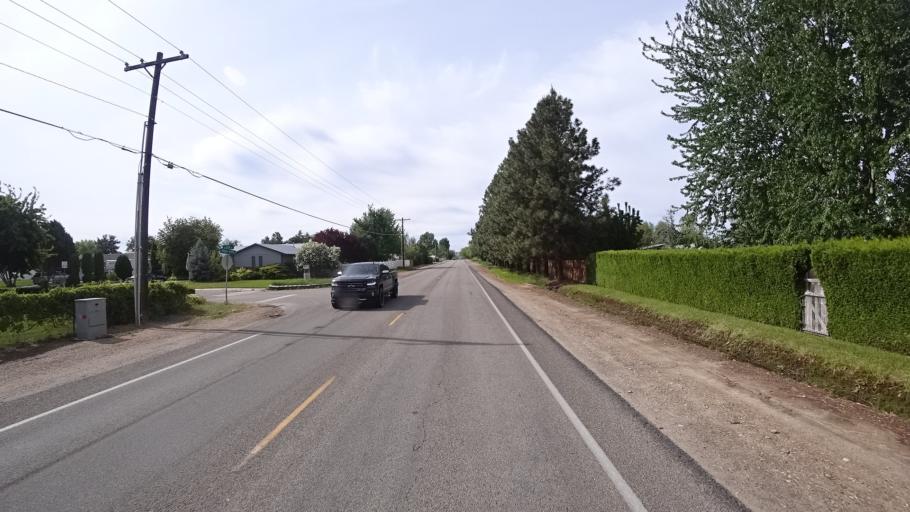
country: US
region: Idaho
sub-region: Ada County
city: Garden City
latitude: 43.5573
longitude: -116.2942
